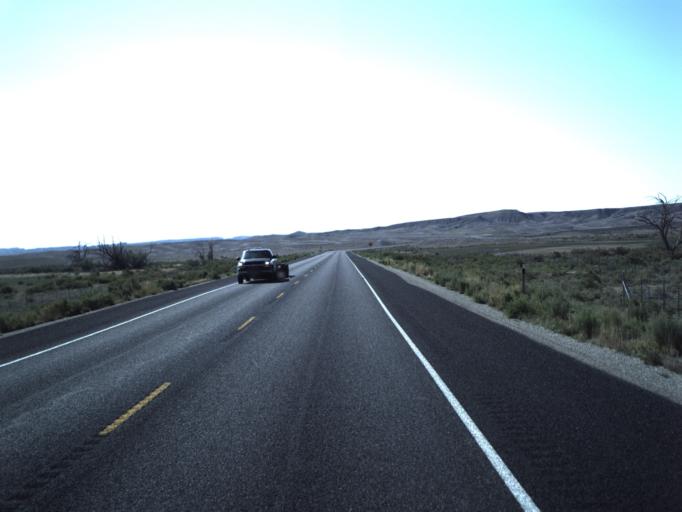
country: US
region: Utah
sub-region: Emery County
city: Ferron
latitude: 39.0566
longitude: -111.1265
